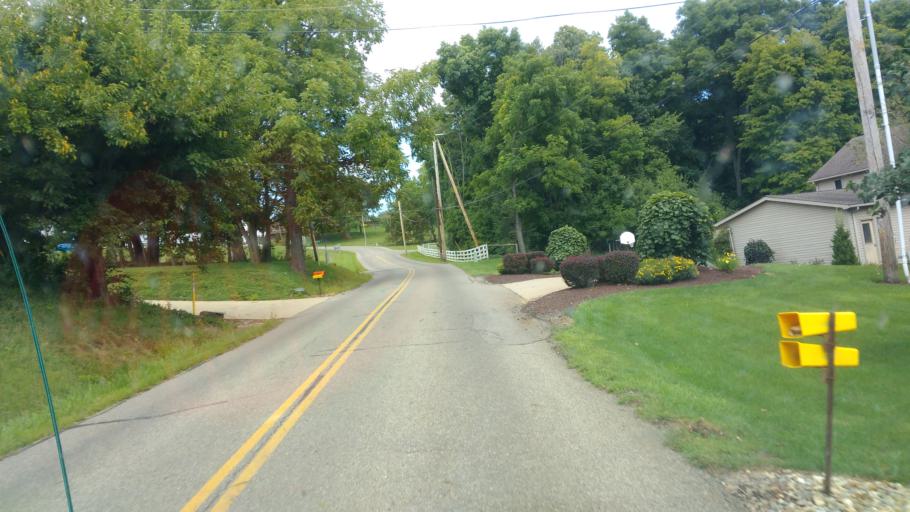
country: US
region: Ohio
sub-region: Holmes County
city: Millersburg
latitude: 40.5567
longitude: -81.8060
